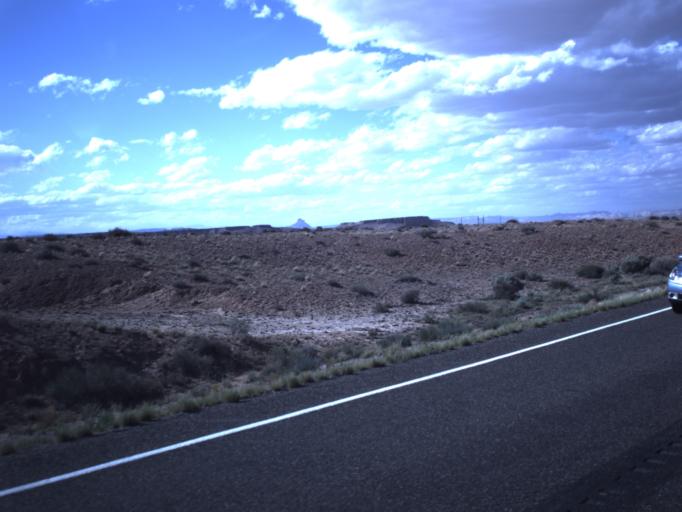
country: US
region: Utah
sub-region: Emery County
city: Ferron
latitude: 38.2990
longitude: -110.6684
